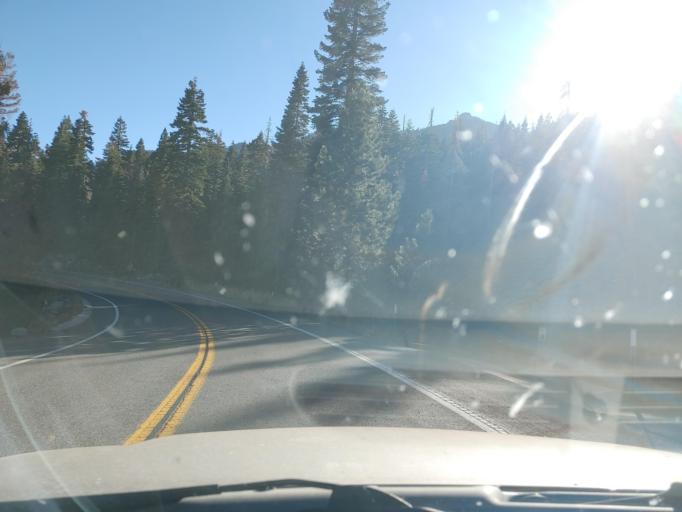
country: US
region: California
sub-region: Placer County
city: Tahoma
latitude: 39.0075
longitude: -120.1173
